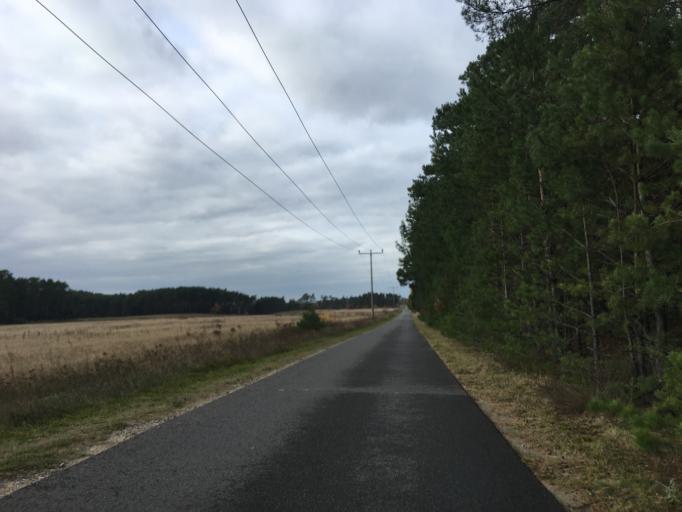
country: DE
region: Brandenburg
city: Jamlitz
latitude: 52.0806
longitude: 14.4527
